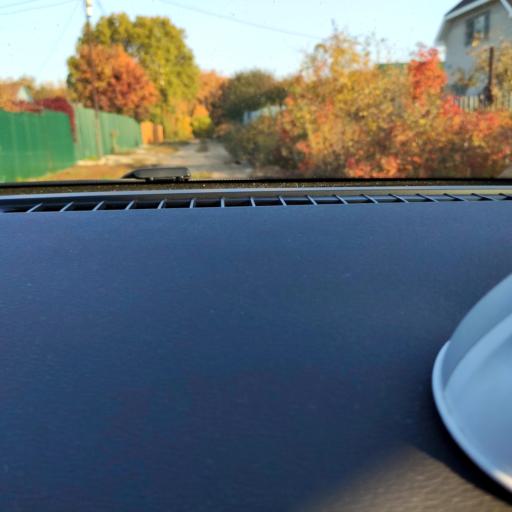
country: RU
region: Samara
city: Petra-Dubrava
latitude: 53.2592
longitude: 50.2742
